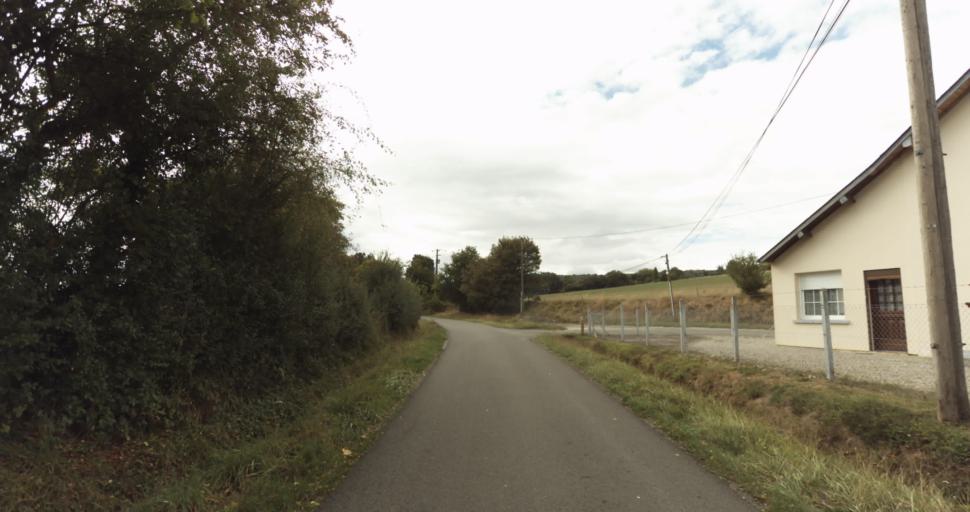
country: FR
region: Lower Normandy
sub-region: Departement de l'Orne
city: Gace
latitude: 48.7757
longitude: 0.3492
